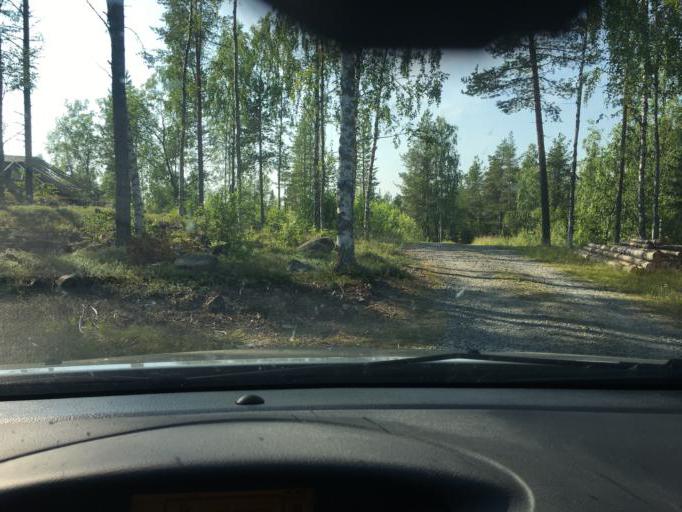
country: SE
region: Norrbotten
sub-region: Kalix Kommun
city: Toere
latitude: 65.8687
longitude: 22.6426
